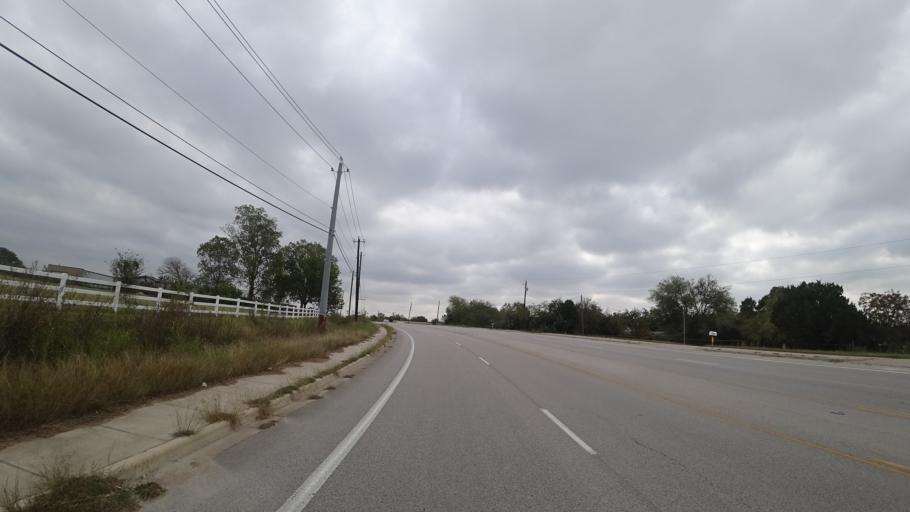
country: US
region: Texas
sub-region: Travis County
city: Pflugerville
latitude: 30.3919
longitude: -97.6274
